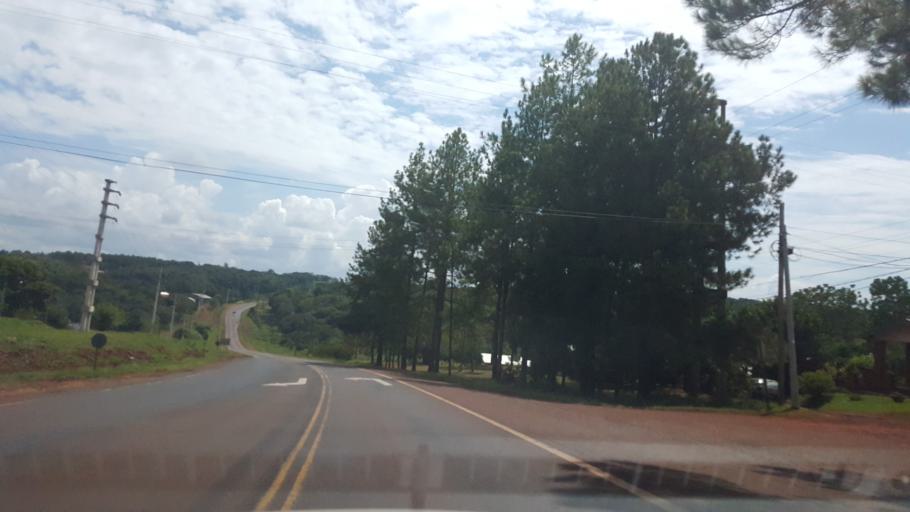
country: AR
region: Misiones
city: Capiovi
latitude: -26.8650
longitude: -55.0451
